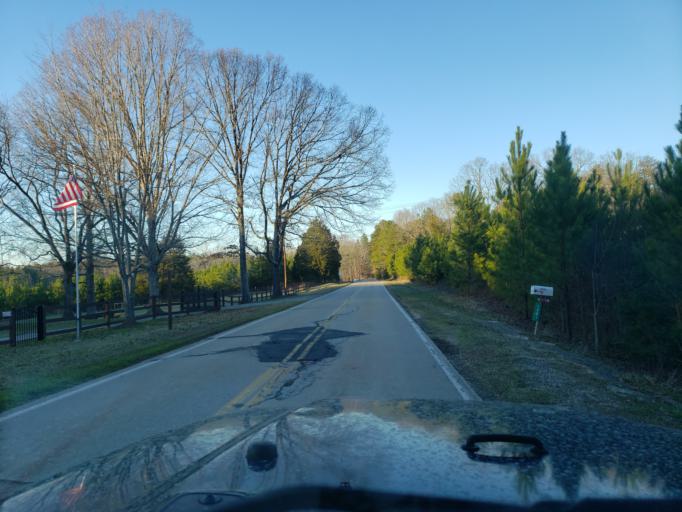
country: US
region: South Carolina
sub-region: Cherokee County
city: Blacksburg
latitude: 35.0440
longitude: -81.4132
